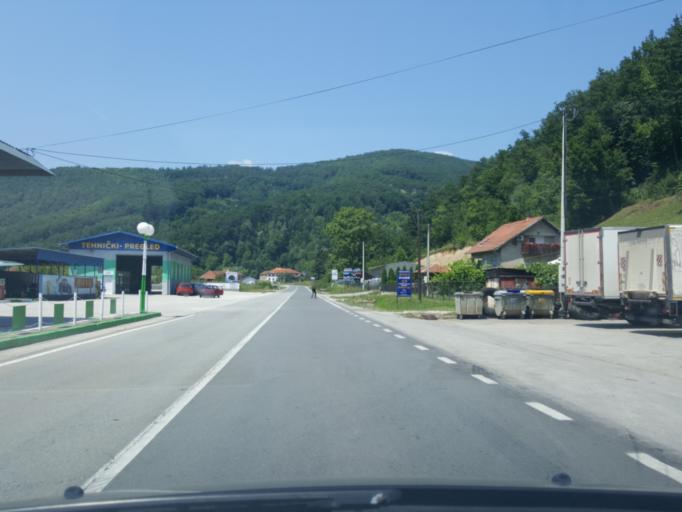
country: RS
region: Central Serbia
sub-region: Moravicki Okrug
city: Gornji Milanovac
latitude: 44.0013
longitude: 20.4390
